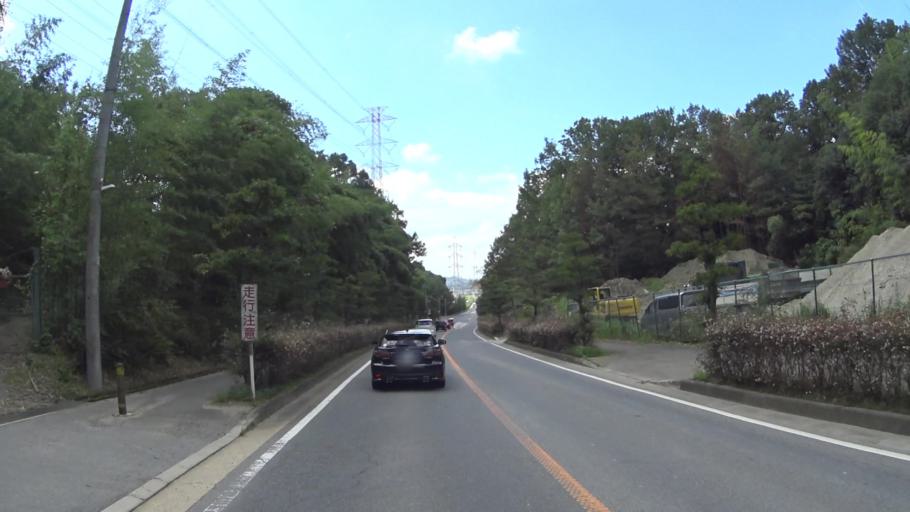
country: JP
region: Kyoto
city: Tanabe
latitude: 34.8490
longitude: 135.7909
